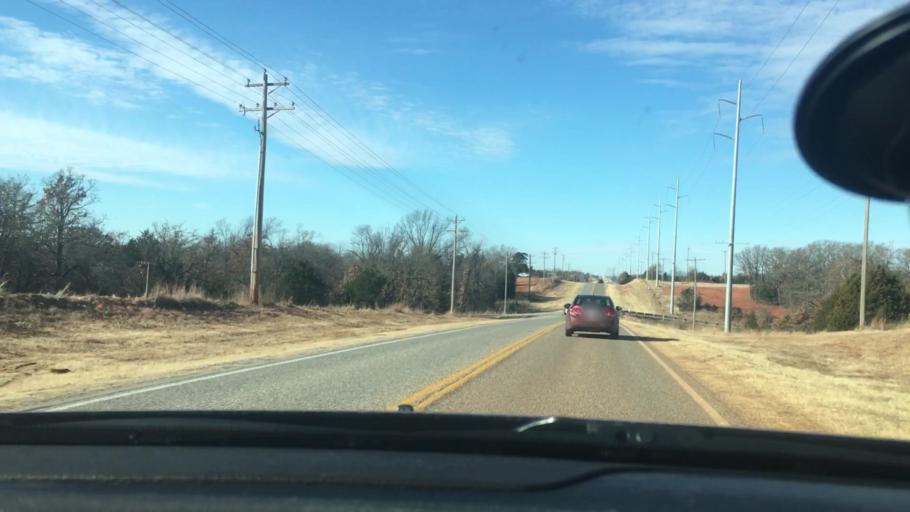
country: US
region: Oklahoma
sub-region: Cleveland County
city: Lexington
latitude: 35.0150
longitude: -97.1931
